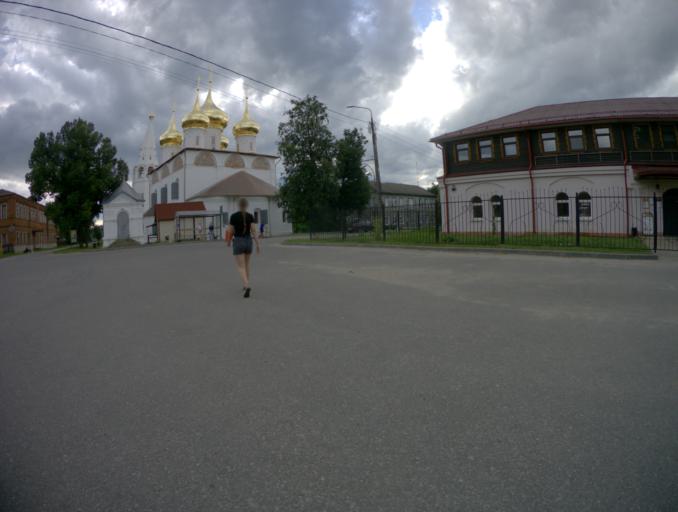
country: RU
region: Vladimir
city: Gorokhovets
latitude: 56.2069
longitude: 42.6773
